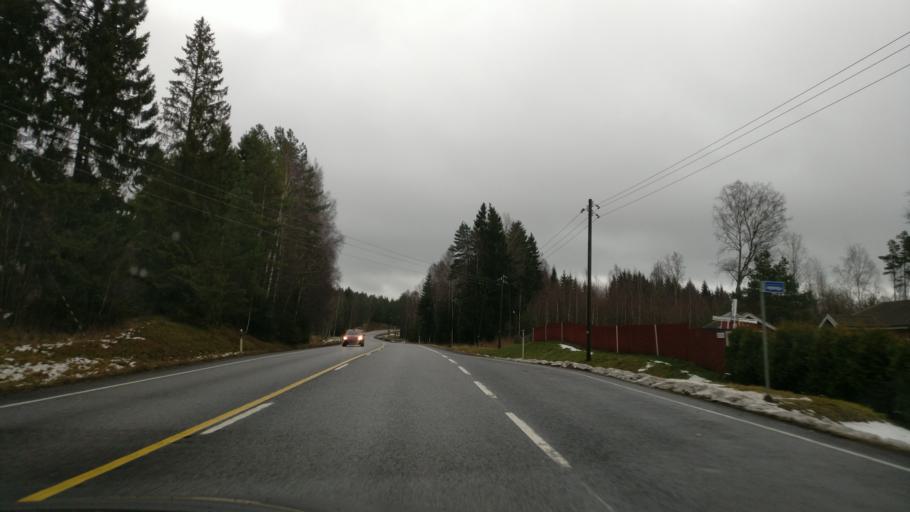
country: FI
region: Uusimaa
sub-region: Raaseporin
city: Ekenaes
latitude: 59.9500
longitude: 23.3580
